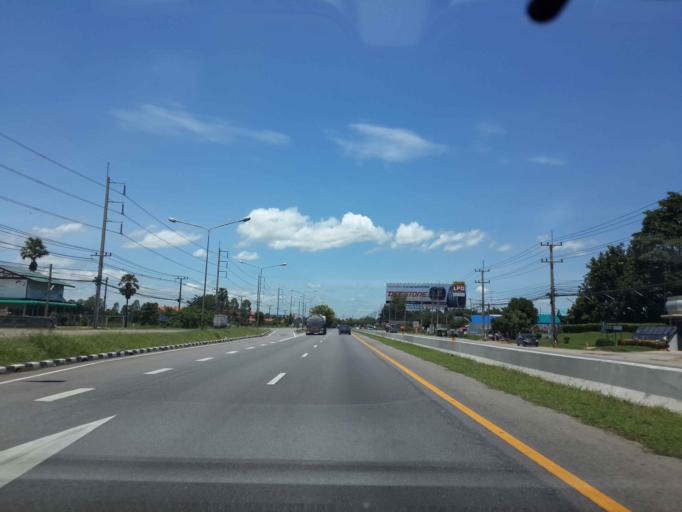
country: TH
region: Phetchaburi
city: Khao Yoi
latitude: 13.2670
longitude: 99.8215
